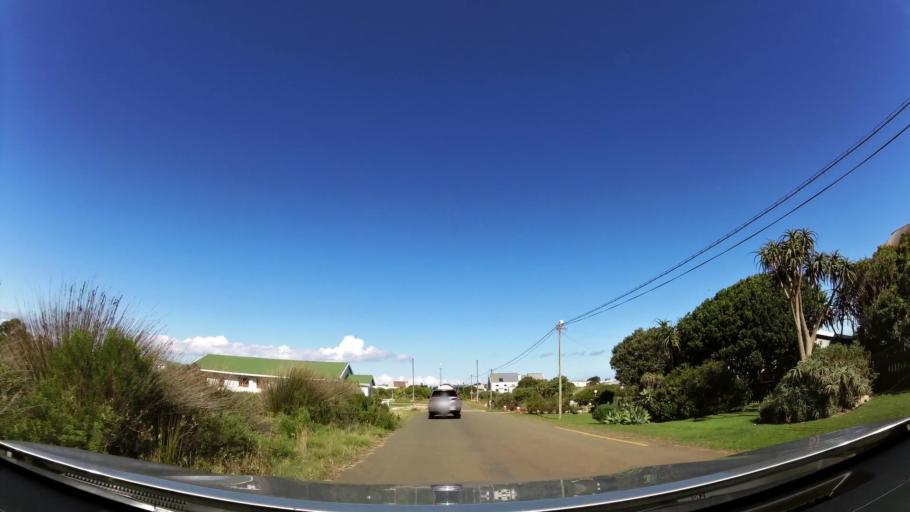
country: ZA
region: Western Cape
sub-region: Overberg District Municipality
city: Grabouw
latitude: -34.3671
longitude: 18.8909
